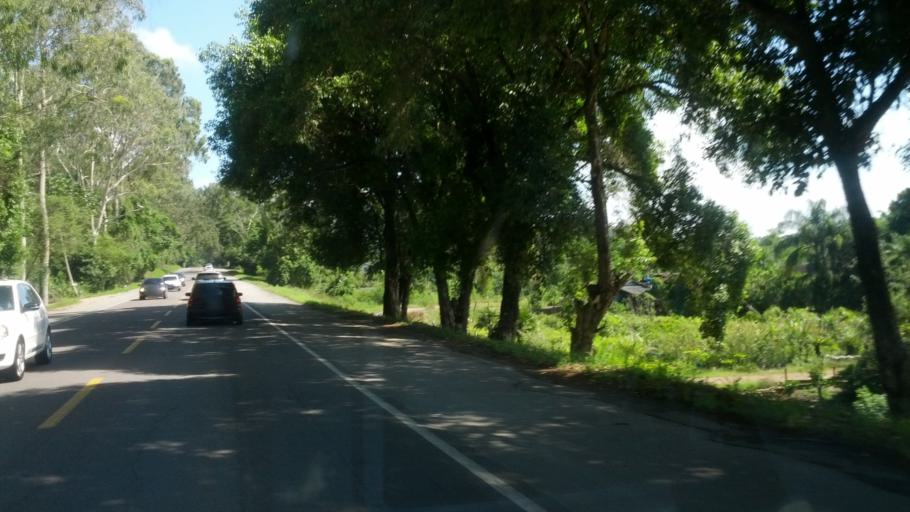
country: BR
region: Santa Catarina
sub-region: Rio Do Sul
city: Rio do Sul
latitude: -27.1562
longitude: -49.5565
